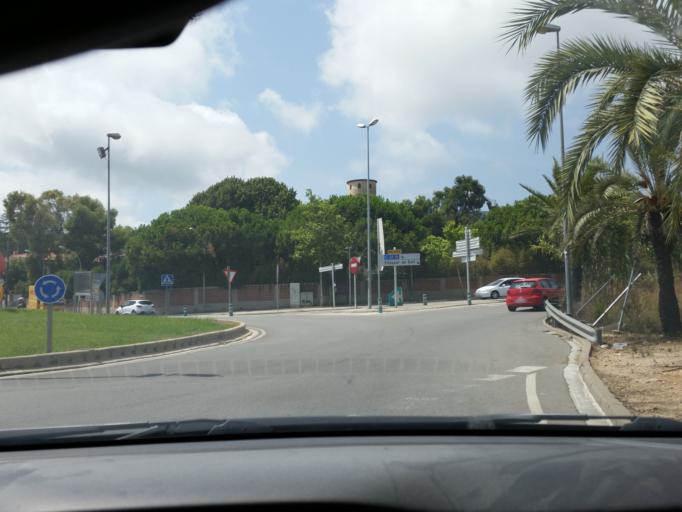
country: ES
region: Catalonia
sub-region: Provincia de Barcelona
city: Premia de Mar
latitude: 41.5022
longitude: 2.3599
